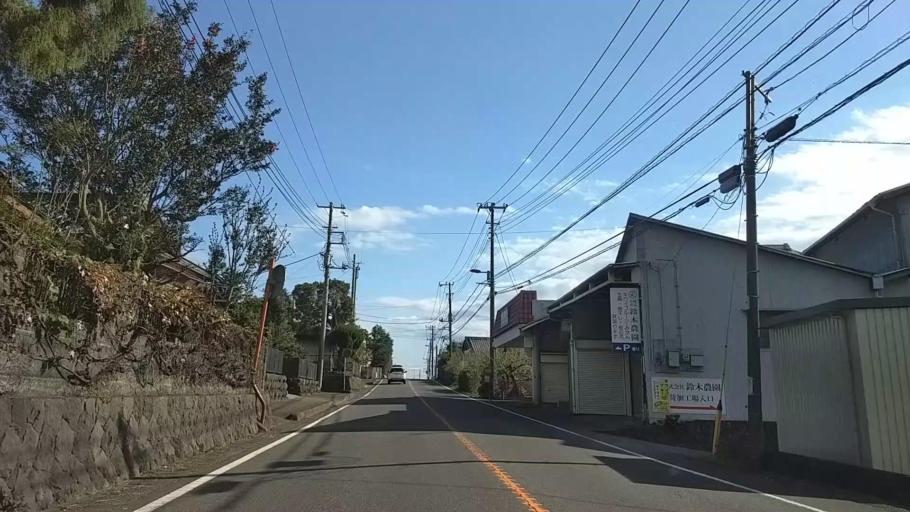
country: JP
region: Kanagawa
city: Odawara
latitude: 35.3150
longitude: 139.1740
